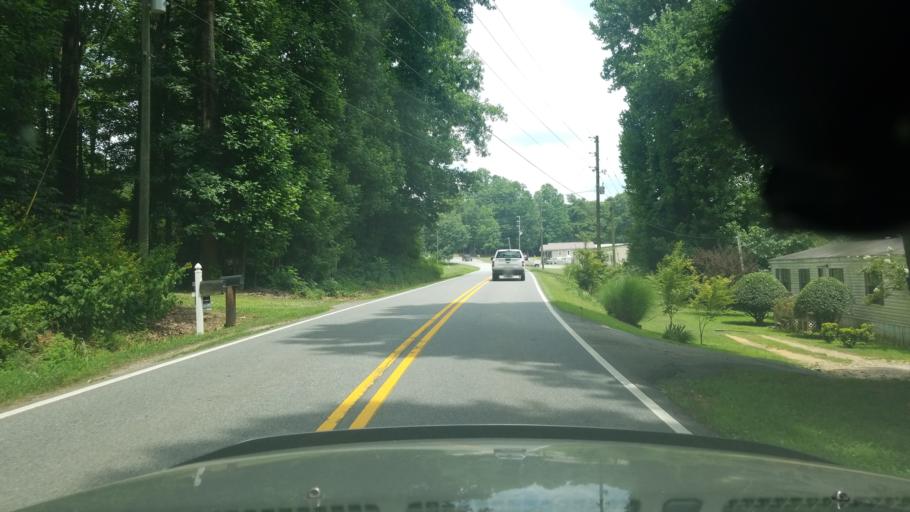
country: US
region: Georgia
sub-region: Forsyth County
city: Cumming
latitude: 34.2127
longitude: -84.2062
